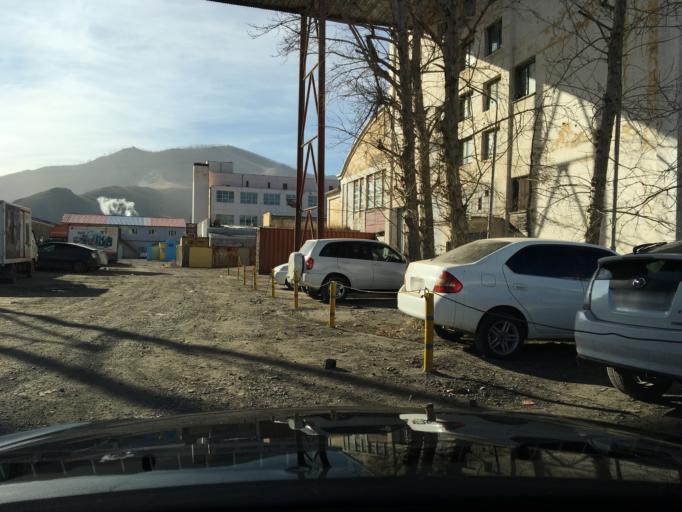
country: MN
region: Ulaanbaatar
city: Ulaanbaatar
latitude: 47.8937
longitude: 106.8918
